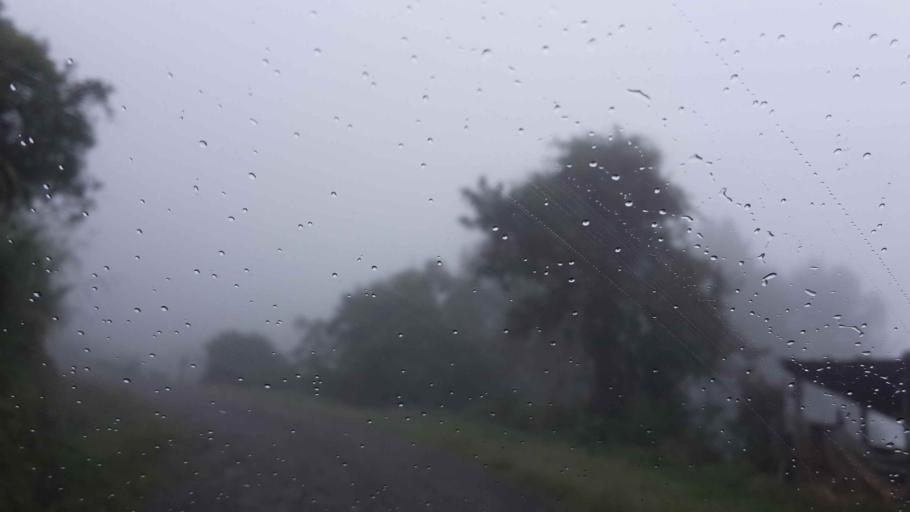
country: BO
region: Cochabamba
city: Colomi
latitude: -17.0868
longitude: -65.9971
